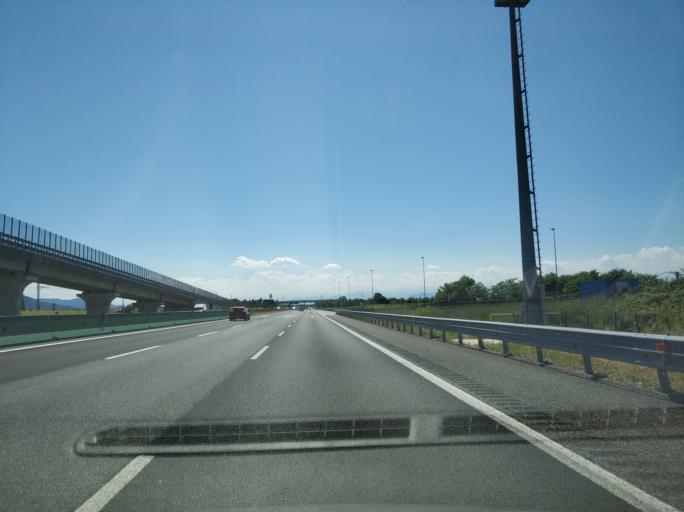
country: IT
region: Piedmont
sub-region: Provincia di Torino
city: Chivasso
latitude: 45.2218
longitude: 7.9184
